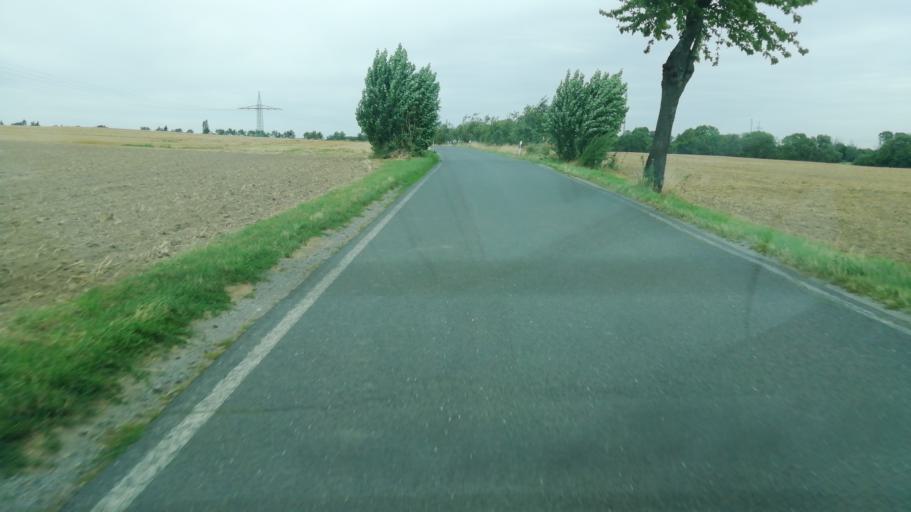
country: DE
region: Saxony
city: Wilsdruff
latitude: 51.0678
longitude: 13.5961
